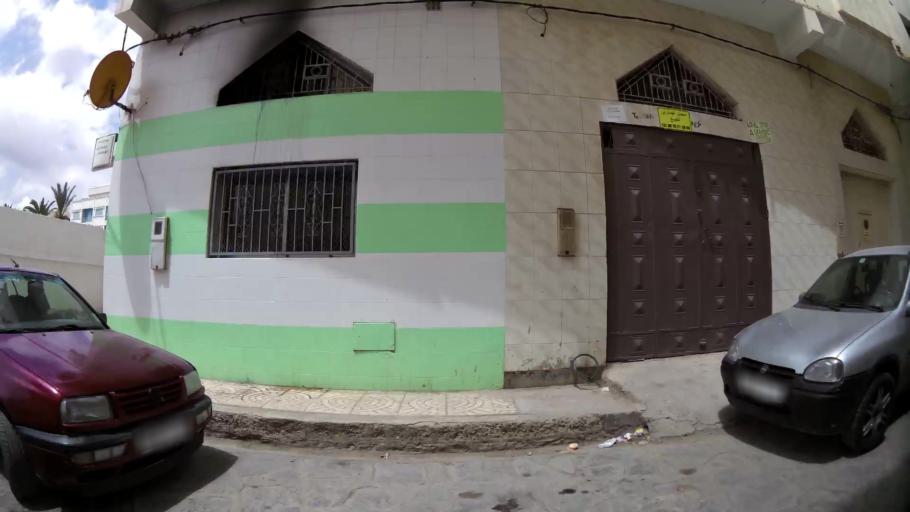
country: MA
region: Oriental
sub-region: Nador
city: Nador
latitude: 35.1725
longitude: -2.9239
